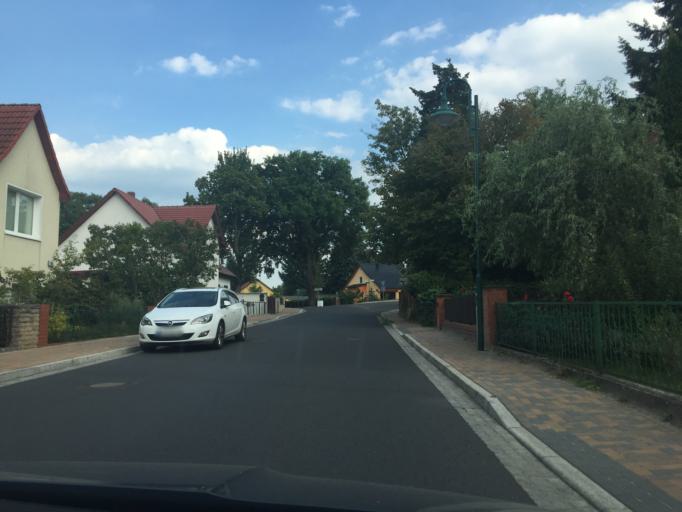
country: DE
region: Brandenburg
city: Erkner
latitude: 52.3863
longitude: 13.7488
